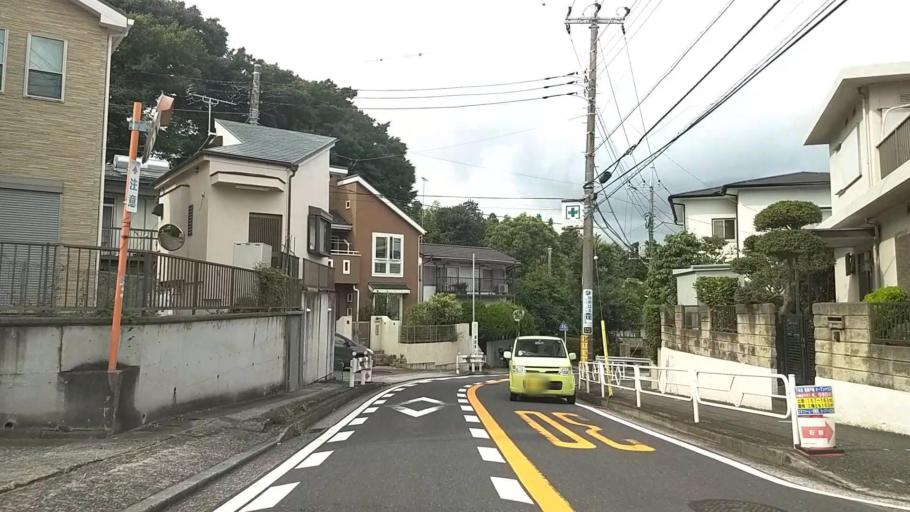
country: JP
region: Kanagawa
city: Yokohama
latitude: 35.4123
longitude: 139.5551
